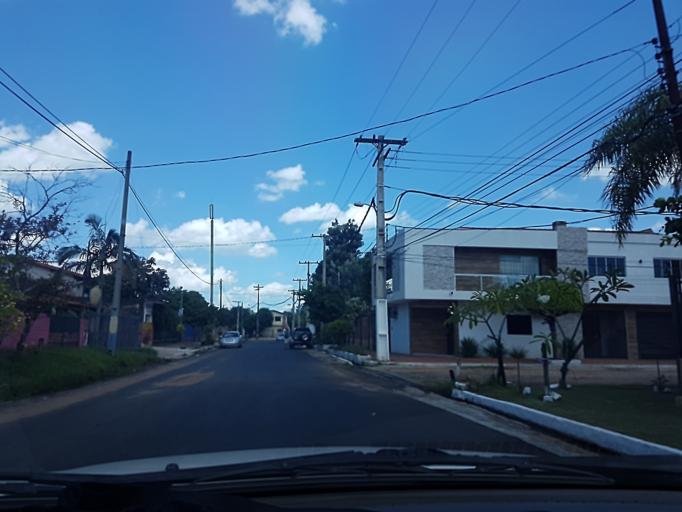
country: PY
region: Central
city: San Lorenzo
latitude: -25.2630
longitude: -57.5006
